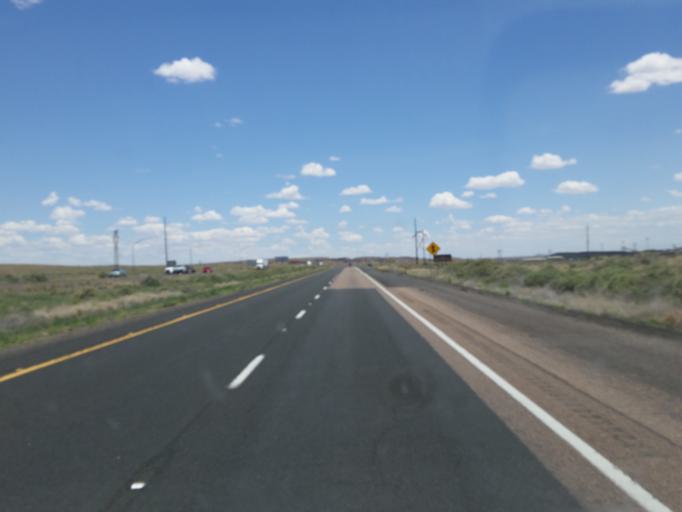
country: US
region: Arizona
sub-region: Navajo County
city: Joseph City
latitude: 34.9522
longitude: -110.3101
